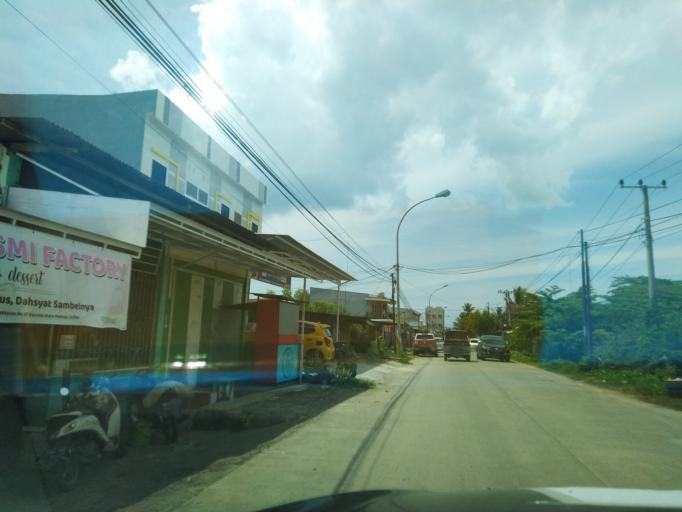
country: ID
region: Sulawesi Barat
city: Mamuju
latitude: -2.6818
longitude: 118.8778
